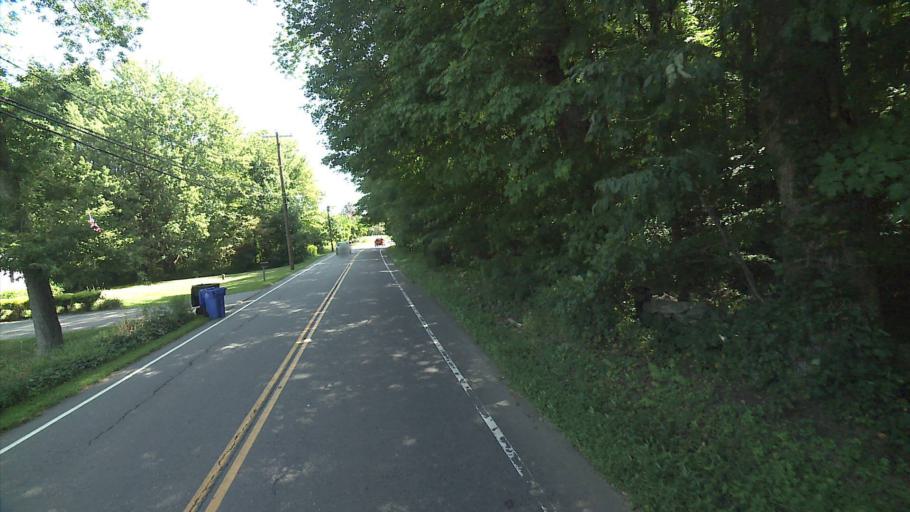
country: US
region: Connecticut
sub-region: New London County
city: Baltic
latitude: 41.6180
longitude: -72.1078
